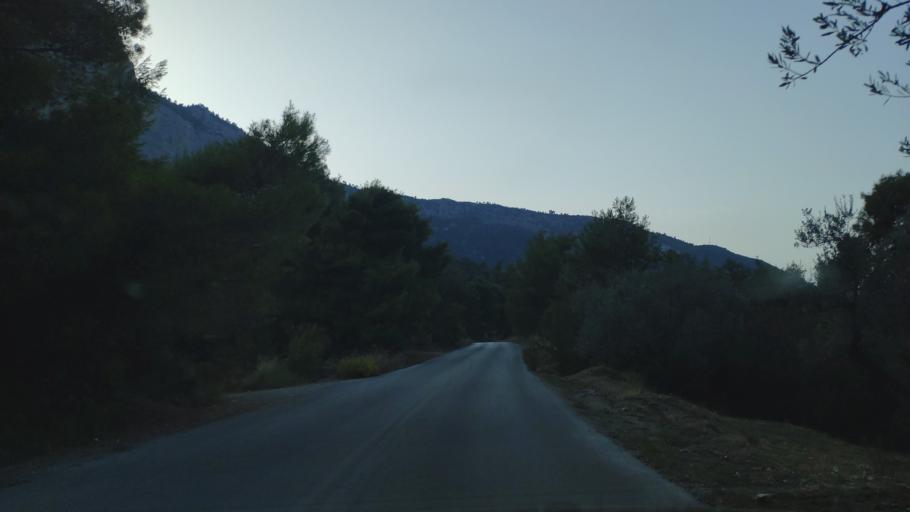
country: GR
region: West Greece
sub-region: Nomos Achaias
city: Aiyira
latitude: 38.0991
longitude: 22.3994
